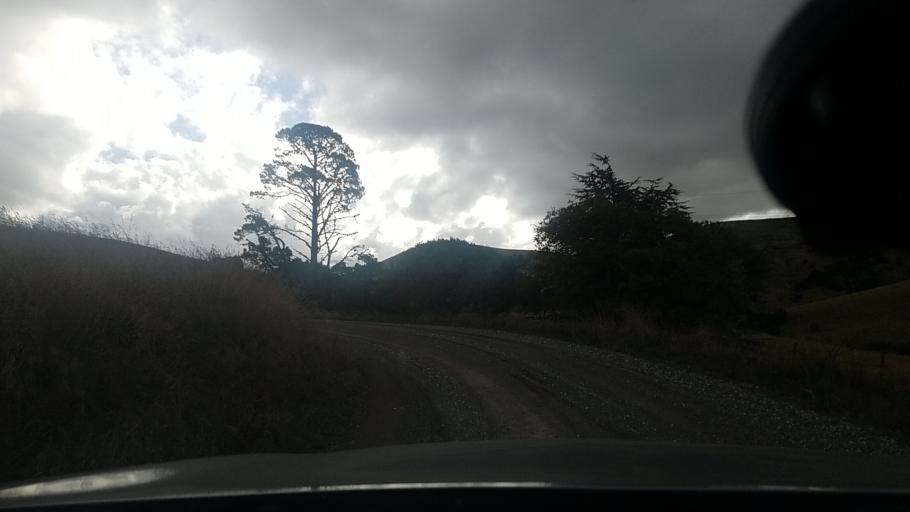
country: NZ
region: Marlborough
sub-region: Marlborough District
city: Blenheim
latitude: -41.5873
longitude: 174.0881
